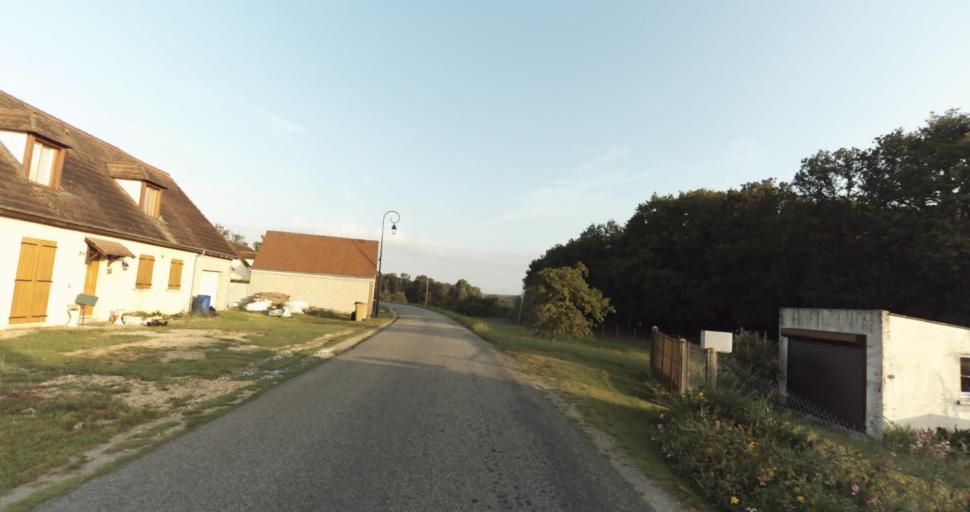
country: FR
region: Haute-Normandie
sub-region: Departement de l'Eure
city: Marcilly-sur-Eure
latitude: 48.7865
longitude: 1.3408
